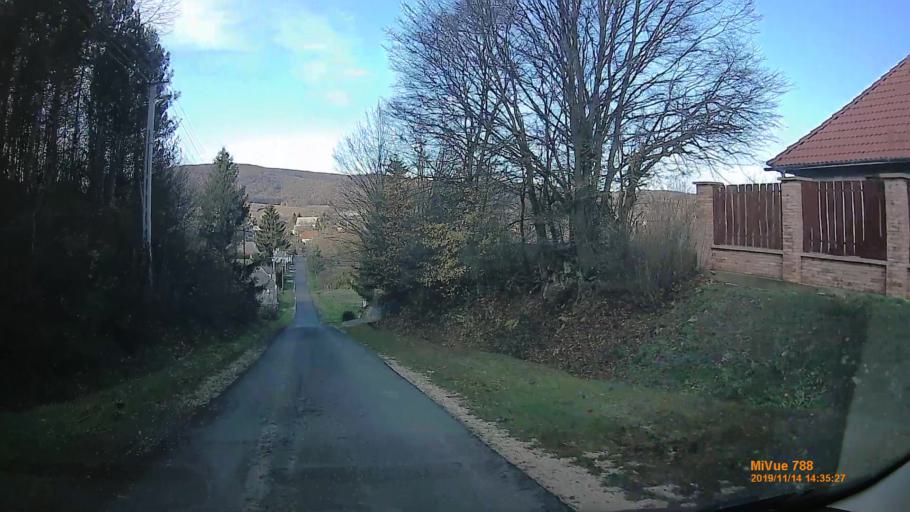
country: HU
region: Veszprem
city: Zirc
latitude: 47.2255
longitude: 17.7907
